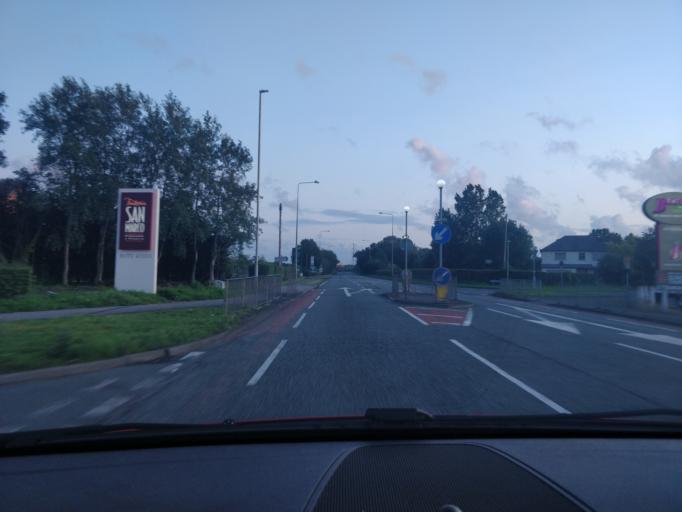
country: GB
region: England
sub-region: Lancashire
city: Tarleton
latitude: 53.6960
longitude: -2.8117
